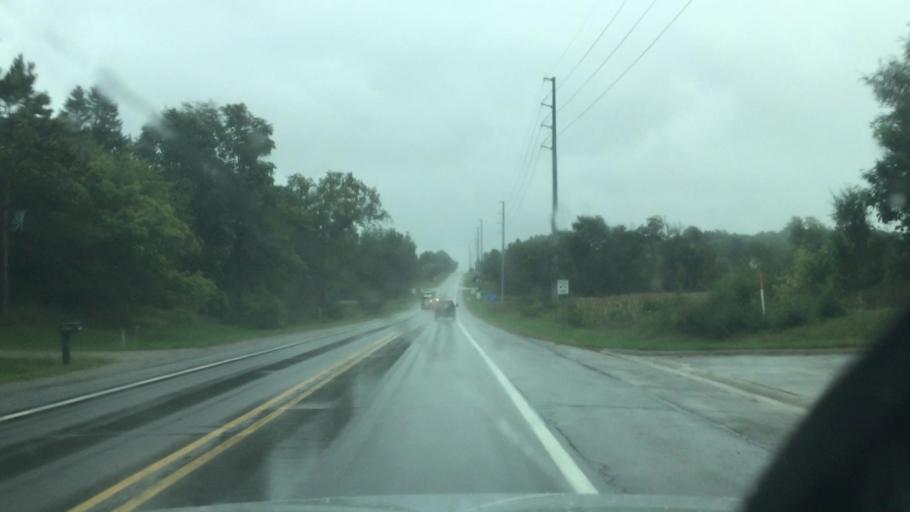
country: US
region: Michigan
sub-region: Livingston County
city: Howell
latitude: 42.6301
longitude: -83.8611
